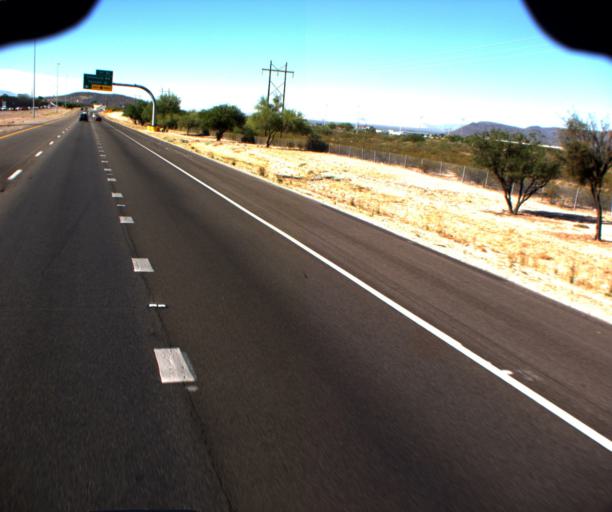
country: US
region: Arizona
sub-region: Pima County
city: Drexel Heights
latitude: 32.1460
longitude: -110.9868
